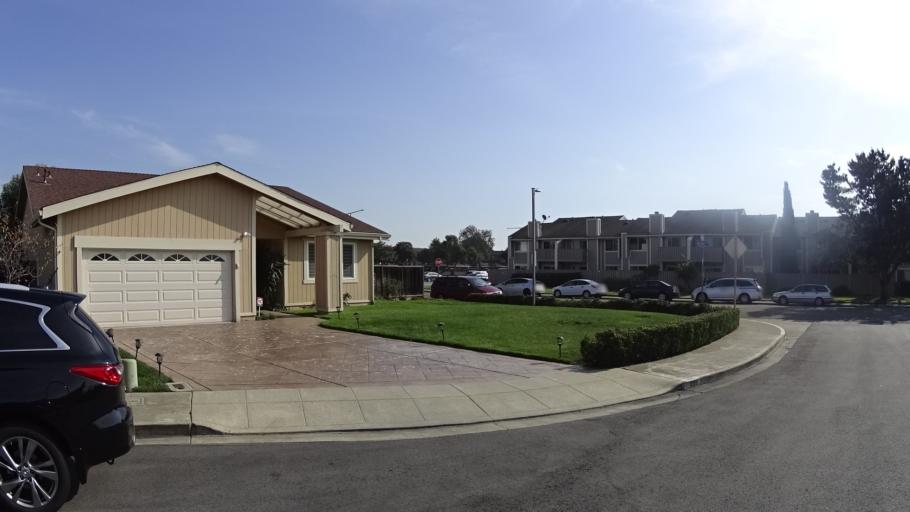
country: US
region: California
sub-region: San Mateo County
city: Foster City
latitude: 37.5527
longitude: -122.2766
